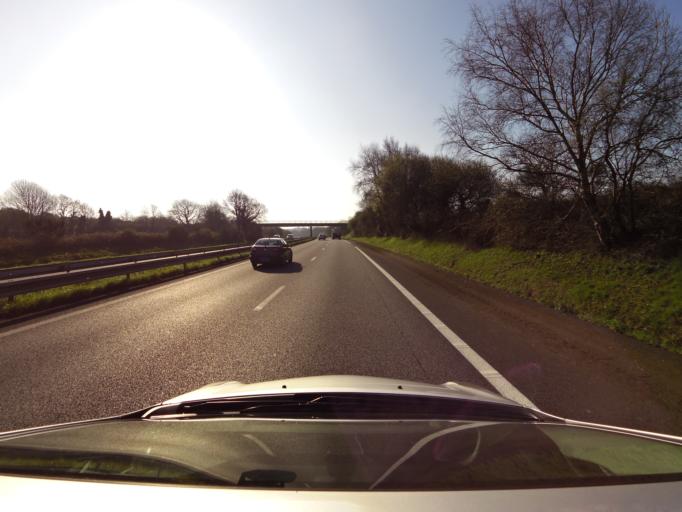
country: FR
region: Brittany
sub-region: Departement du Morbihan
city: Gestel
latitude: 47.7939
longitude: -3.4501
